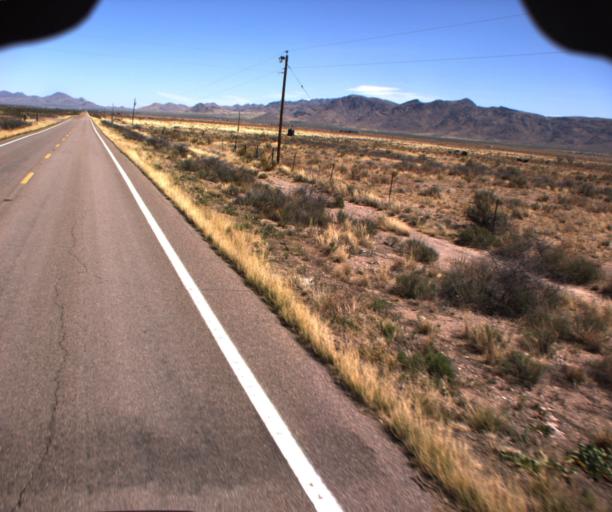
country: US
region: Arizona
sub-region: Cochise County
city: Douglas
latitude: 31.7803
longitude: -109.0704
